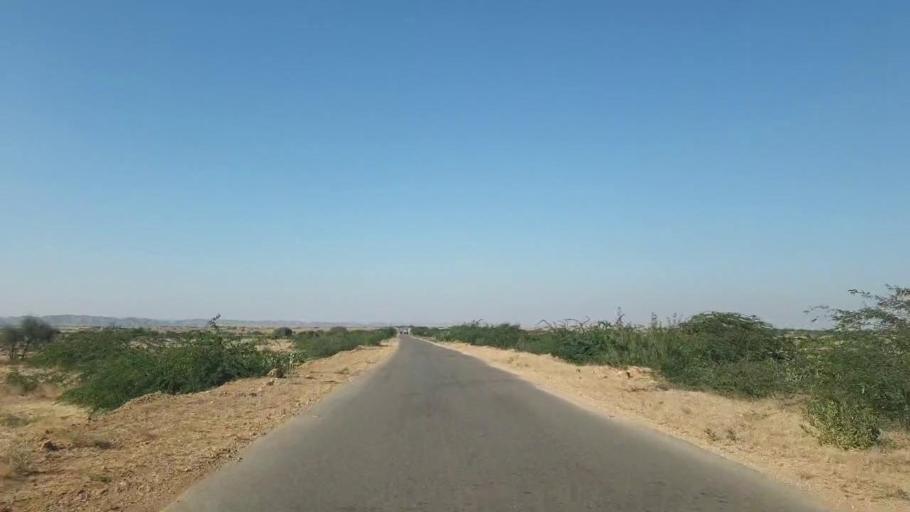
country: PK
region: Sindh
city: Malir Cantonment
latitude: 25.2604
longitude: 67.5998
